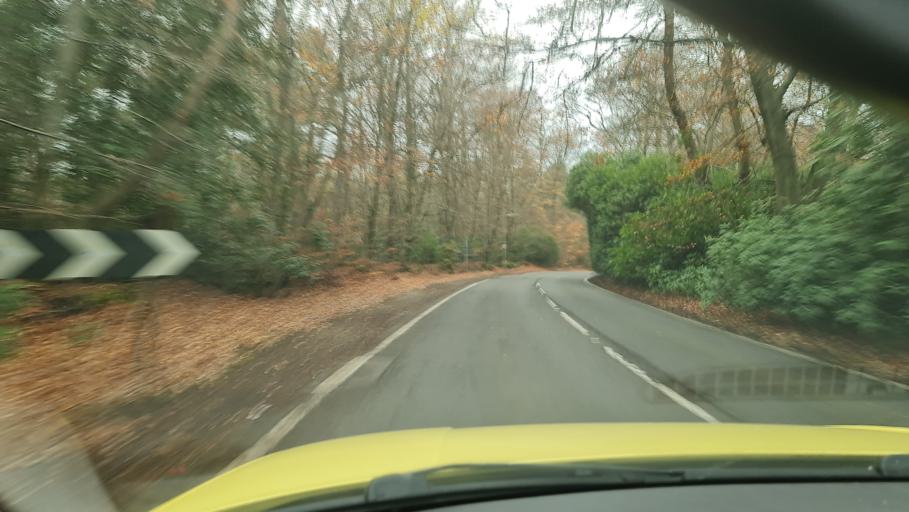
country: GB
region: England
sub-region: Bracknell Forest
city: Sandhurst
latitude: 51.3206
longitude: -0.7813
